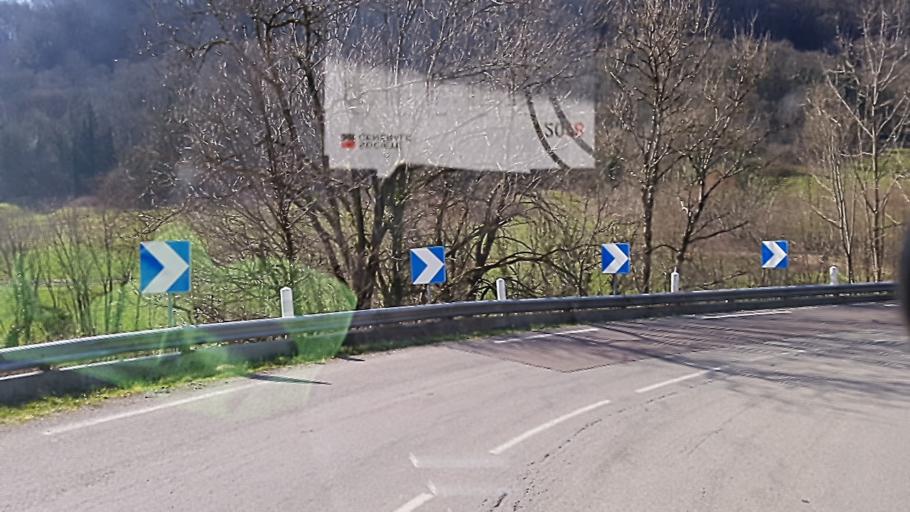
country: FR
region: Franche-Comte
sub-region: Departement du Jura
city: Poligny
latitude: 46.8232
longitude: 5.7283
